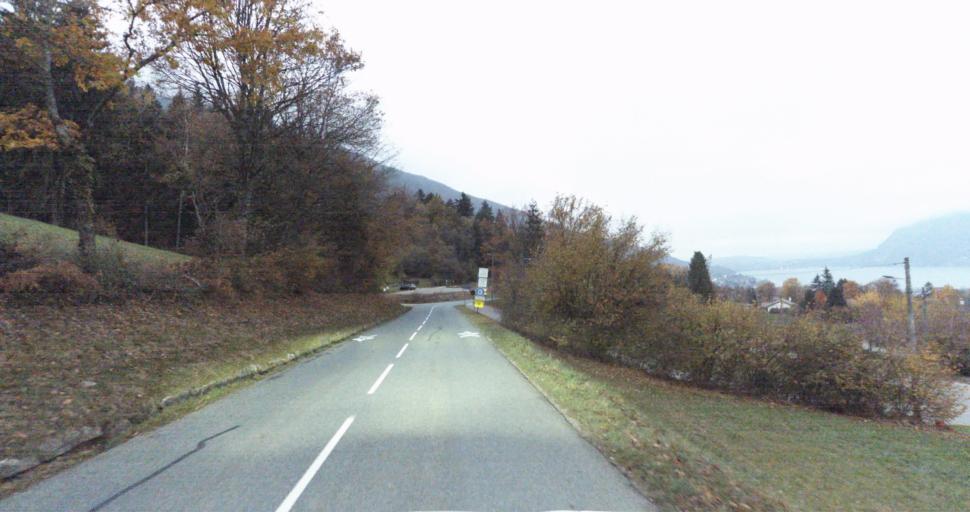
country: FR
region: Rhone-Alpes
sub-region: Departement de la Haute-Savoie
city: Saint-Jorioz
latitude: 45.8378
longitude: 6.1407
